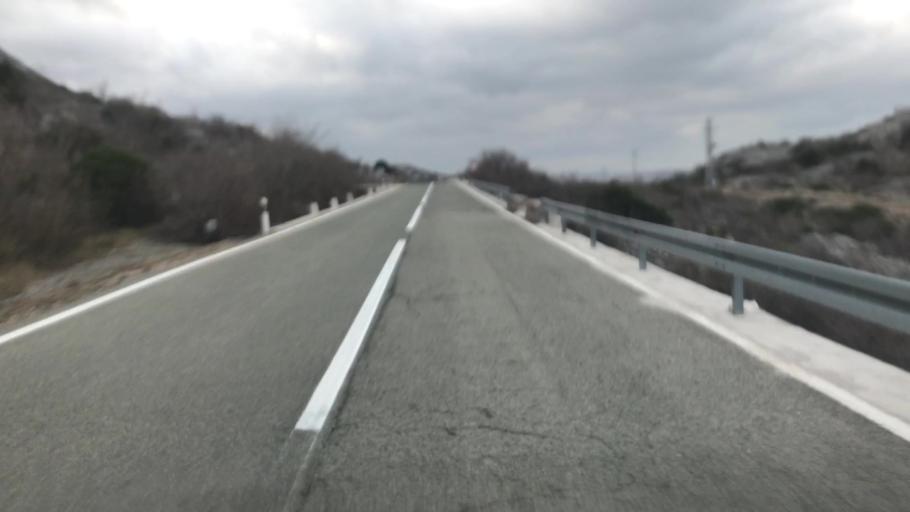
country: HR
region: Licko-Senjska
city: Novalja
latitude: 44.6768
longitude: 14.9414
